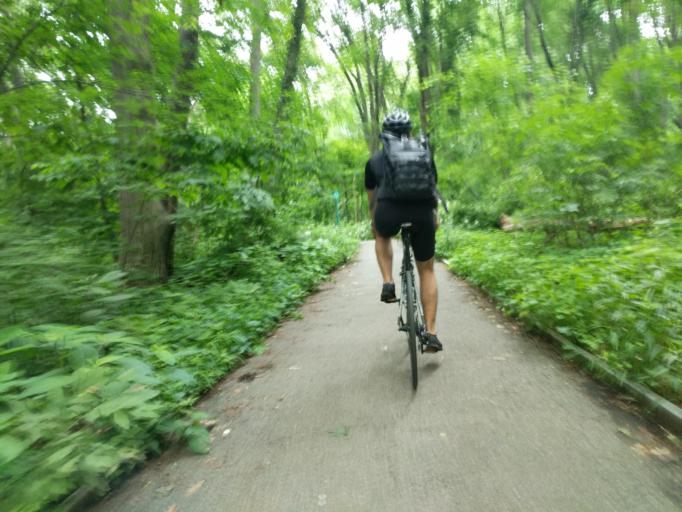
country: US
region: New York
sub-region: Nassau County
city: Bellerose Terrace
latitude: 40.7334
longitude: -73.7704
